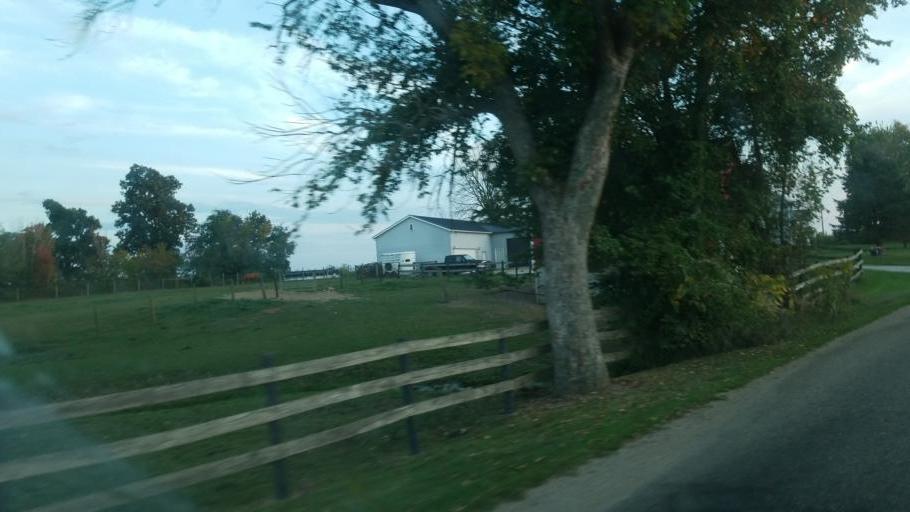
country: US
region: Ohio
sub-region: Knox County
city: Fredericktown
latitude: 40.4424
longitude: -82.5688
